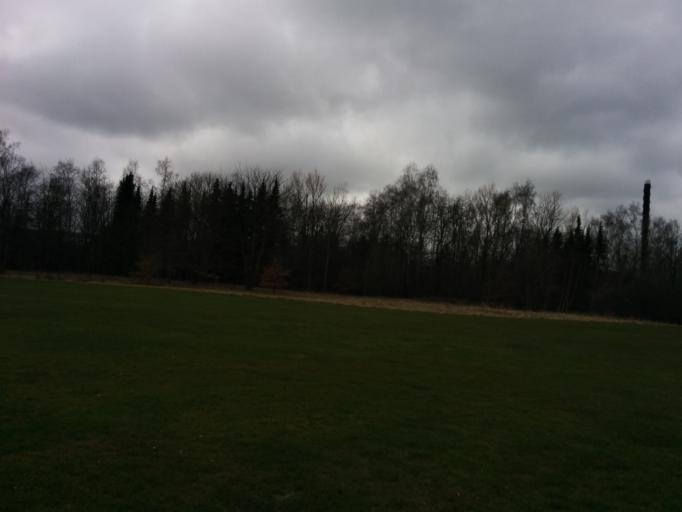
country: DK
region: Capital Region
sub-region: Ballerup Kommune
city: Ballerup
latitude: 55.7173
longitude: 12.3672
